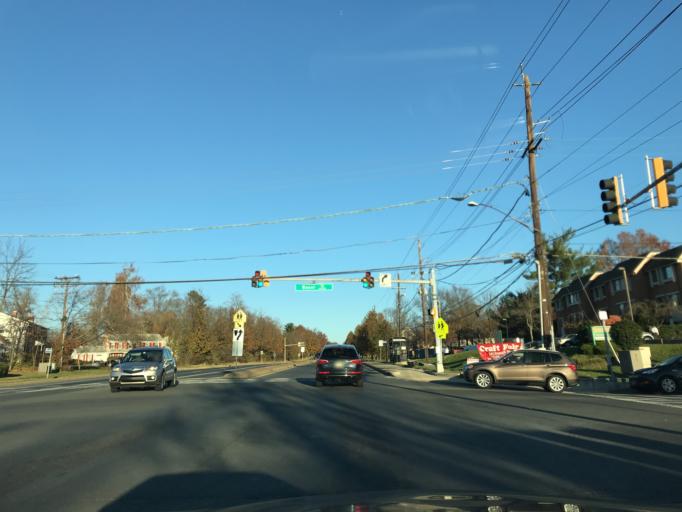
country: US
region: Maryland
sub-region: Montgomery County
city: Rossmoor
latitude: 39.0959
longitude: -77.1103
